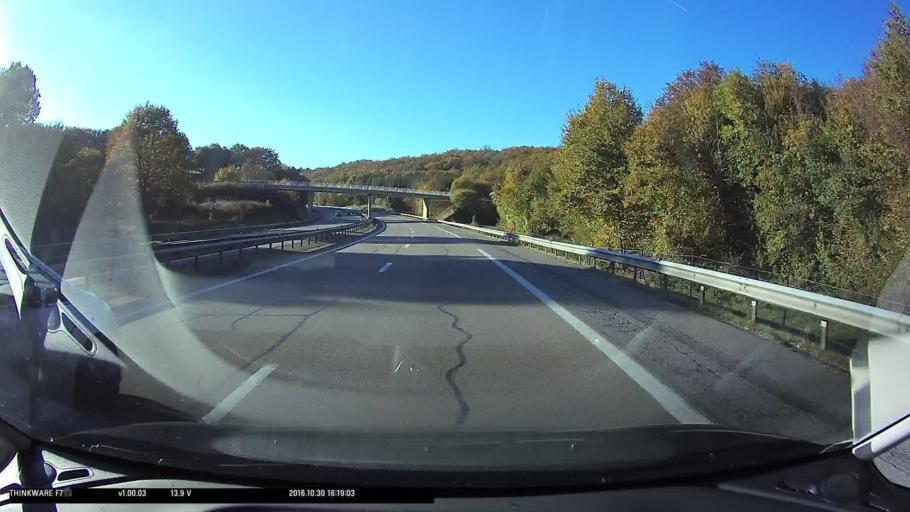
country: FR
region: Franche-Comte
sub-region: Departement du Doubs
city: Clerval
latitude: 47.4074
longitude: 6.4842
